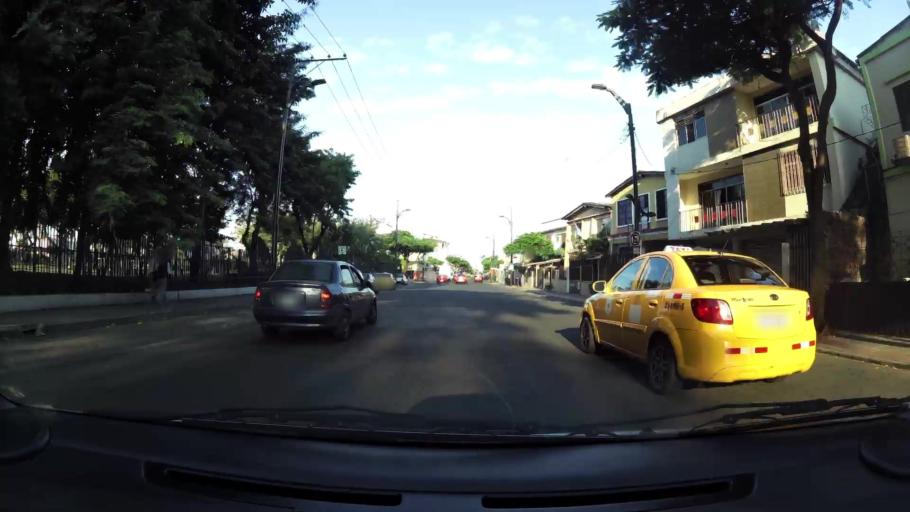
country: EC
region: Guayas
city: Guayaquil
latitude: -2.2134
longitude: -79.8953
